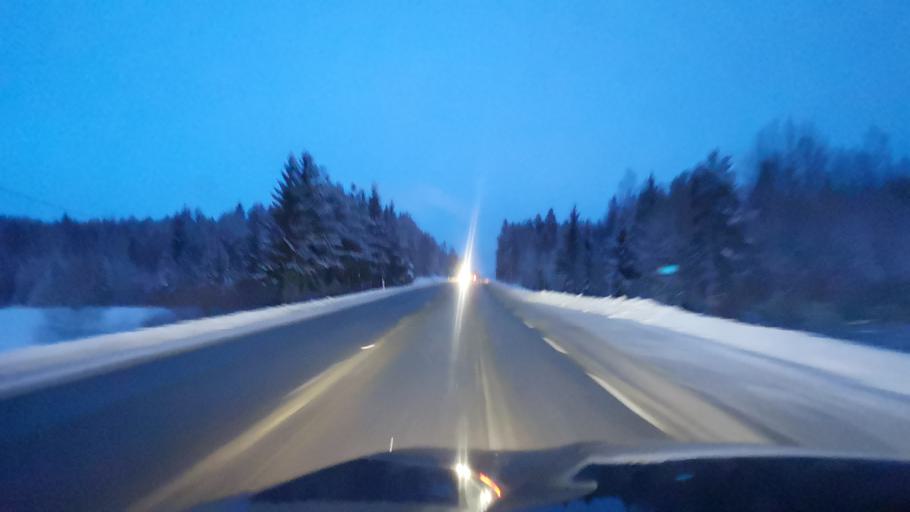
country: FI
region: Varsinais-Suomi
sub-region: Loimaa
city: Loimaa
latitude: 60.8677
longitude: 23.0563
